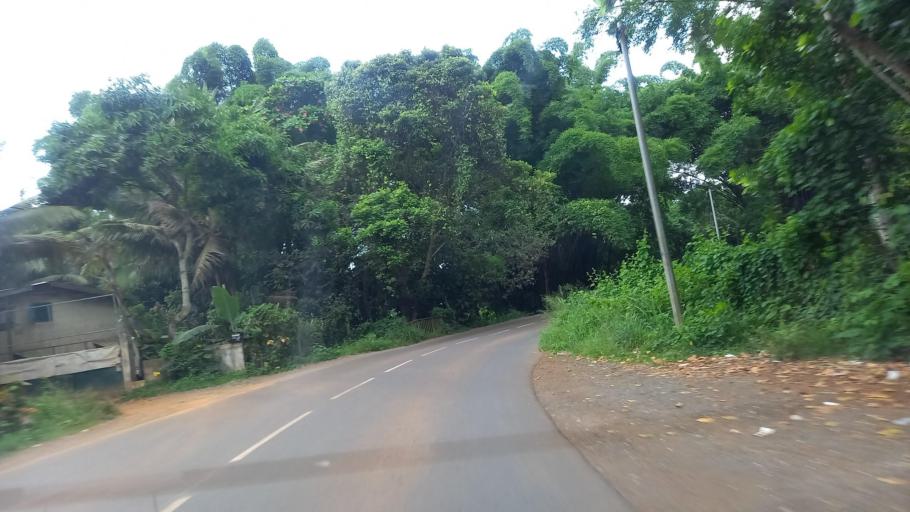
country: YT
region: Ouangani
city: Ouangani
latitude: -12.8323
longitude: 45.1384
